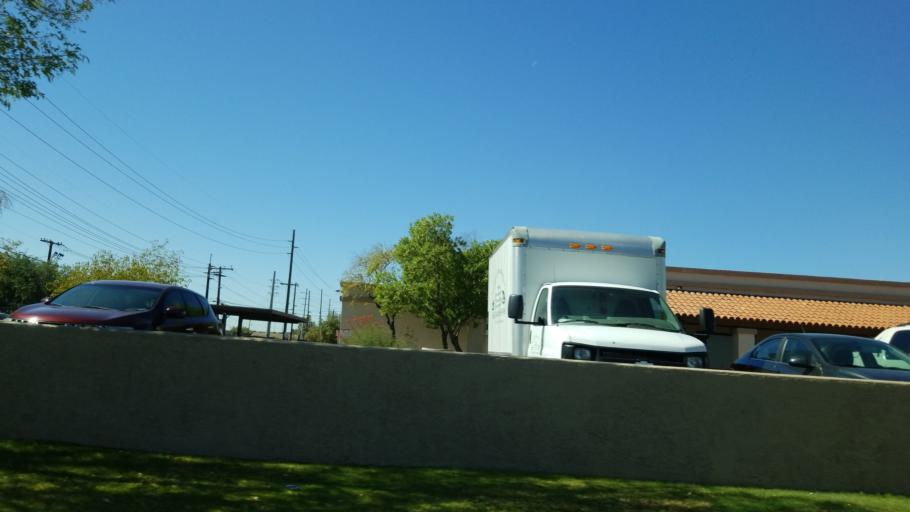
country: US
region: Arizona
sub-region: Maricopa County
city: Phoenix
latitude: 33.4534
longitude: -112.0303
